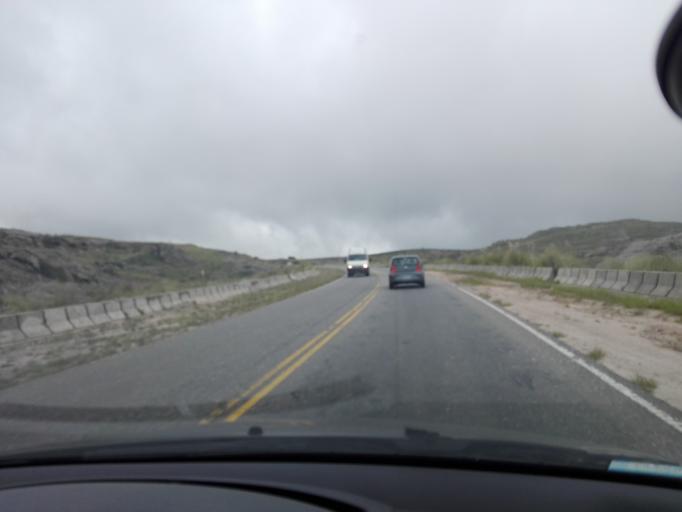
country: AR
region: Cordoba
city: Cuesta Blanca
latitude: -31.6114
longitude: -64.7482
